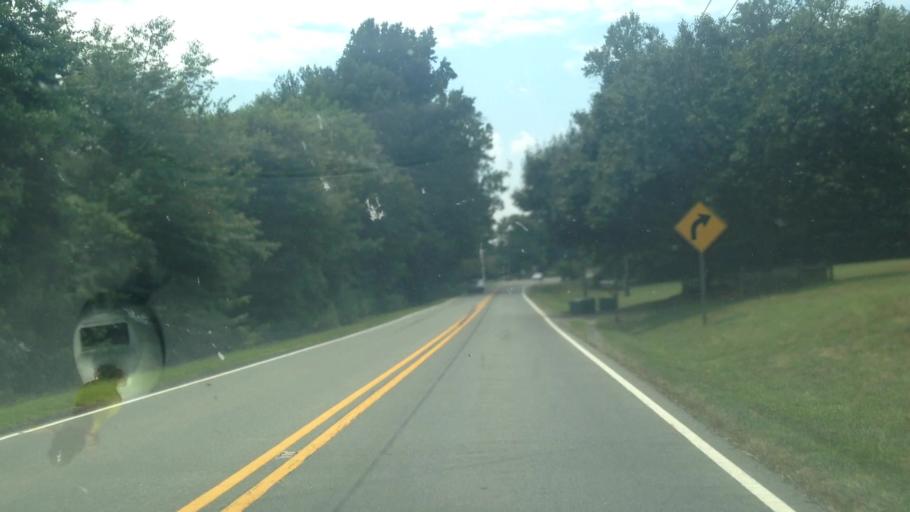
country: US
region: North Carolina
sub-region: Forsyth County
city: Walkertown
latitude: 36.1778
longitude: -80.1828
